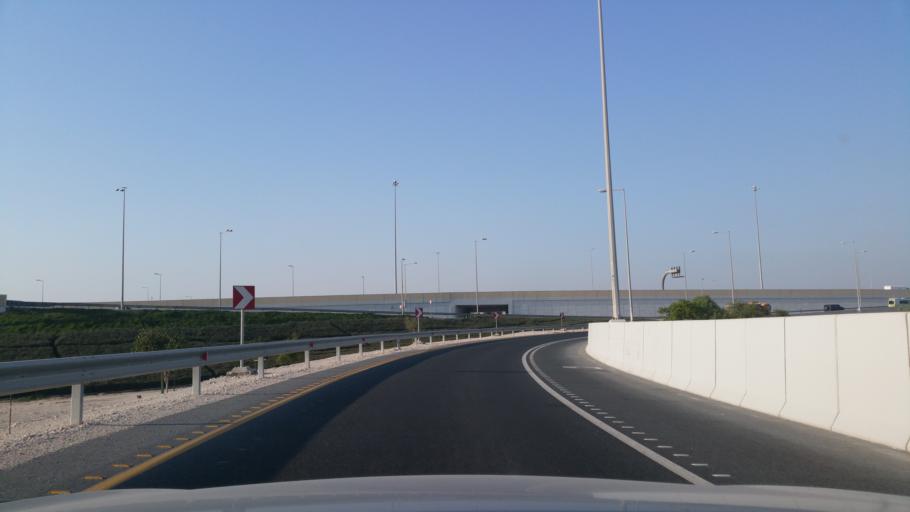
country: QA
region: Al Wakrah
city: Al Wukayr
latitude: 25.1615
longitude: 51.5690
